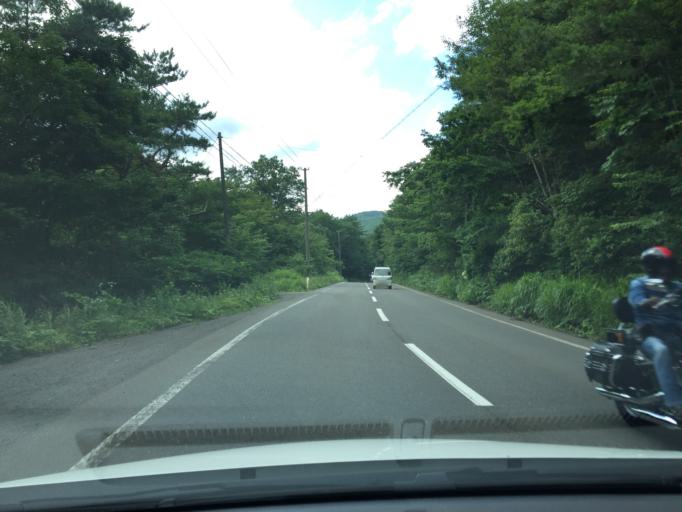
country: JP
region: Fukushima
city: Sukagawa
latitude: 37.2629
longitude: 140.1013
